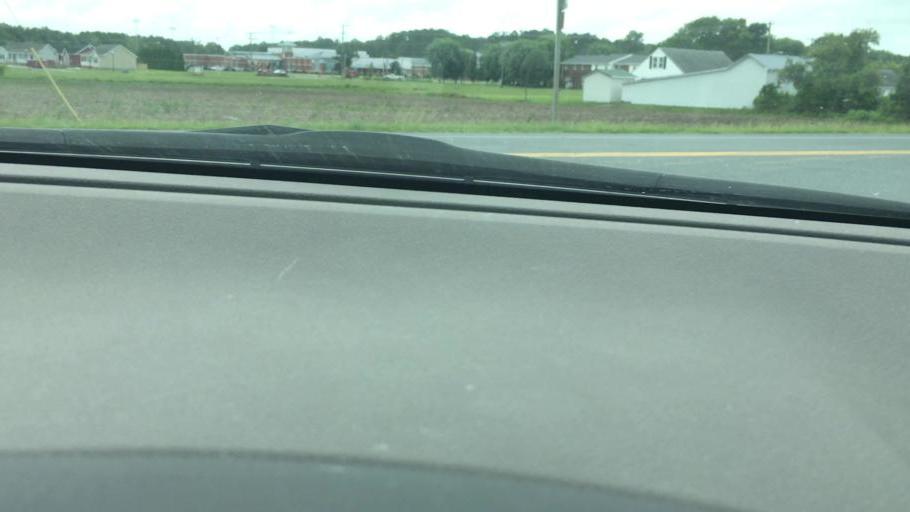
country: US
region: Maryland
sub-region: Worcester County
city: Pocomoke City
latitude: 38.0620
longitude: -75.5494
